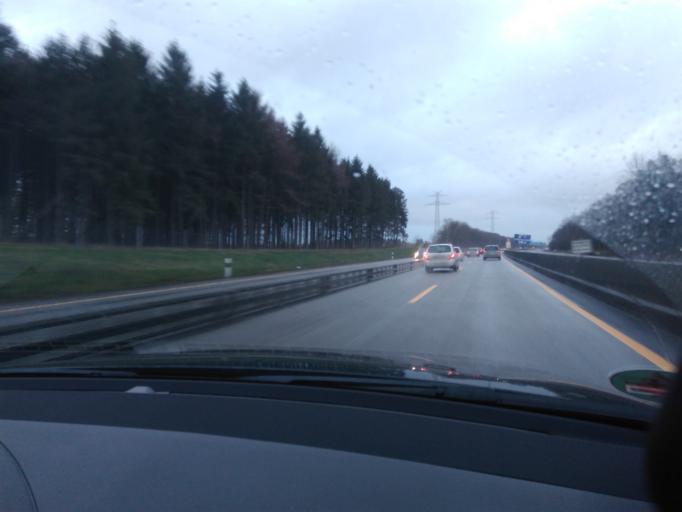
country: DE
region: Schleswig-Holstein
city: Nutzen
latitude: 53.8374
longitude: 9.9271
